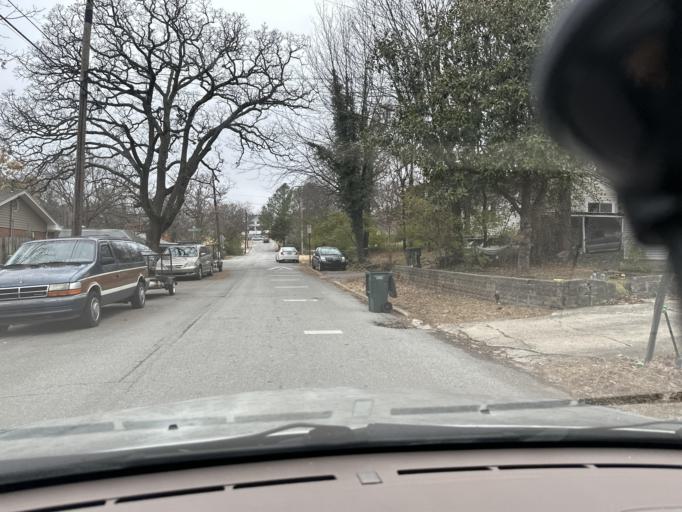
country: US
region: Arkansas
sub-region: Washington County
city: Fayetteville
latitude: 36.0741
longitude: -94.1554
